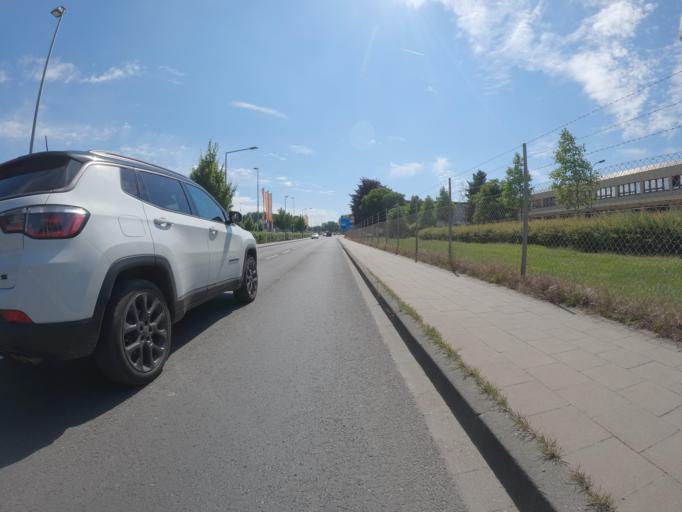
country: DE
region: North Rhine-Westphalia
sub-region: Regierungsbezirk Koln
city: Wurselen
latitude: 50.7580
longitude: 6.1519
